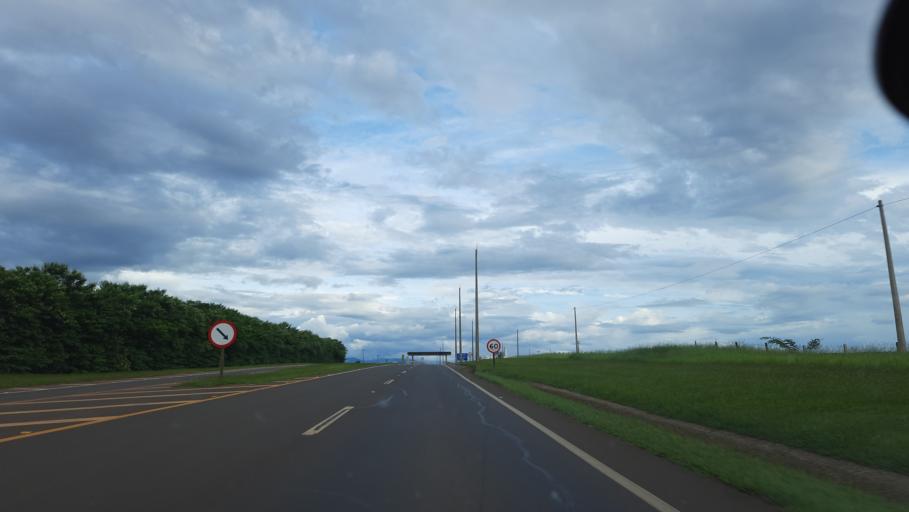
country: BR
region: Sao Paulo
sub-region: Vargem Grande Do Sul
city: Vargem Grande do Sul
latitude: -21.8124
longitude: -46.9881
